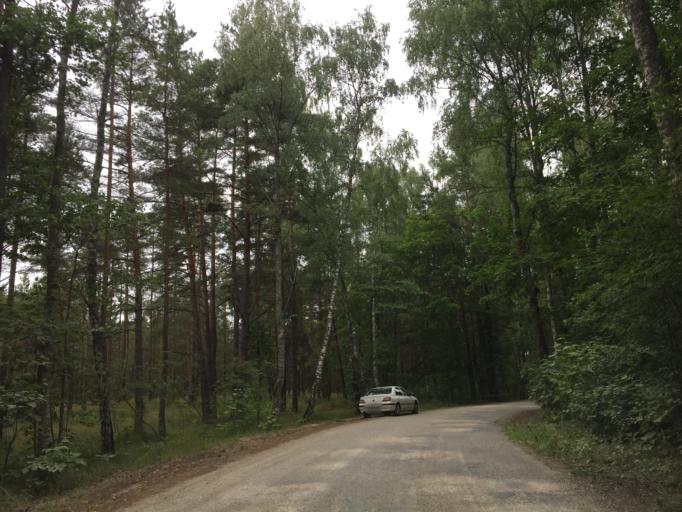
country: LV
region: Riga
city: Jaunciems
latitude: 57.0985
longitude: 24.1875
